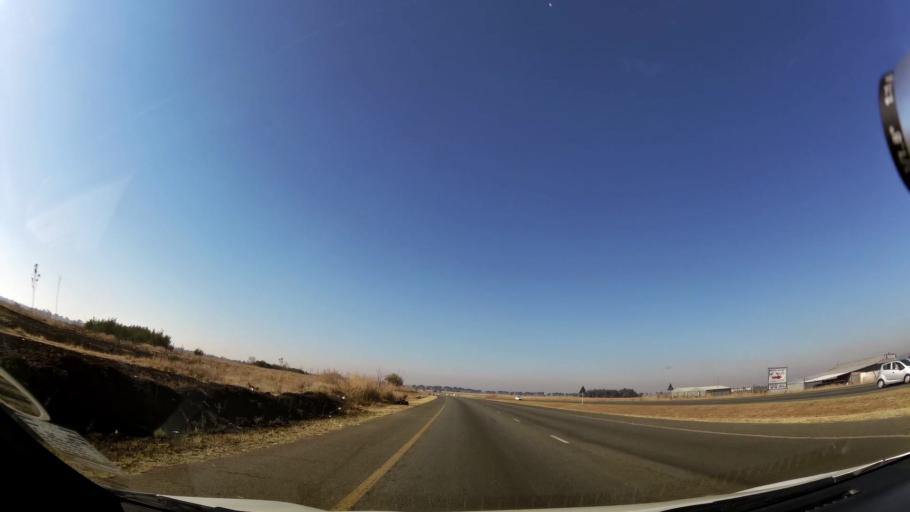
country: ZA
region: Gauteng
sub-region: City of Johannesburg Metropolitan Municipality
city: Johannesburg
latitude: -26.3249
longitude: 28.0690
